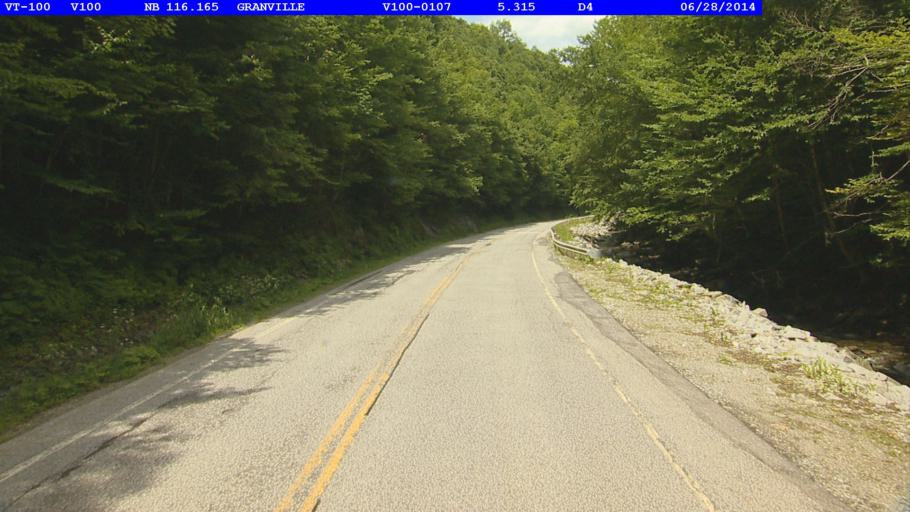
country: US
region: Vermont
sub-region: Orange County
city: Randolph
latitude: 44.0146
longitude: -72.8517
